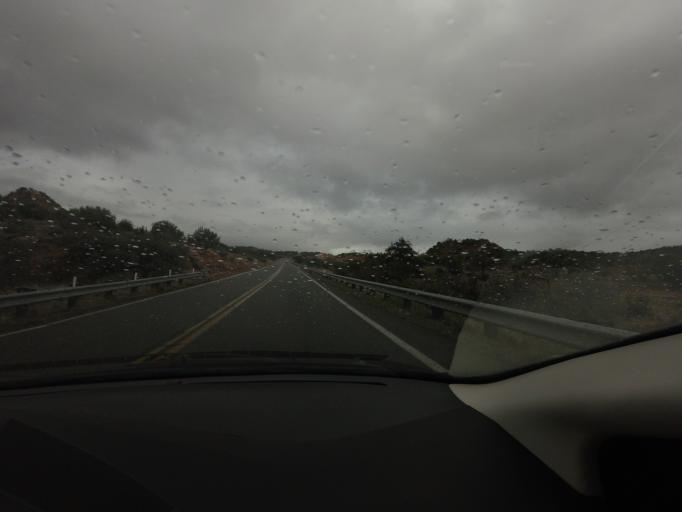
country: US
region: Arizona
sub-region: Yavapai County
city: Cornville
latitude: 34.7005
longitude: -111.8663
